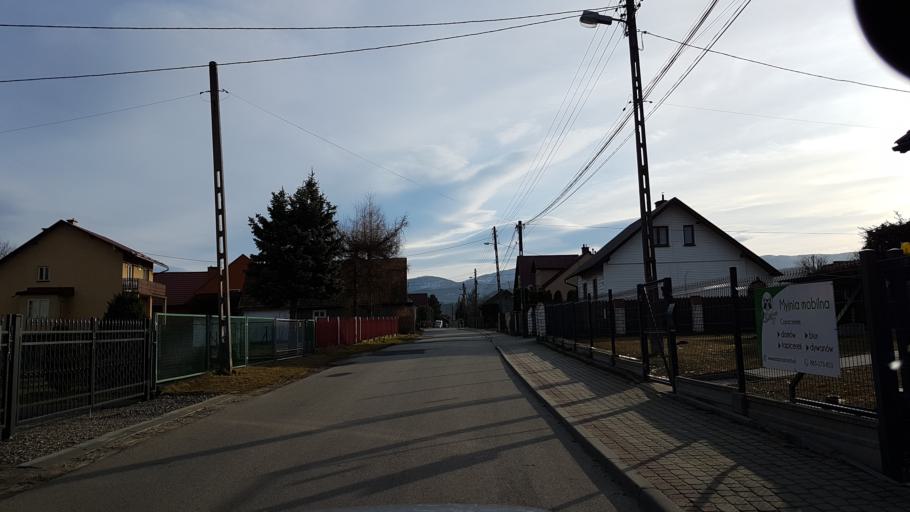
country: PL
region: Lesser Poland Voivodeship
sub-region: Powiat nowosadecki
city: Stary Sacz
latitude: 49.5367
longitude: 20.6556
